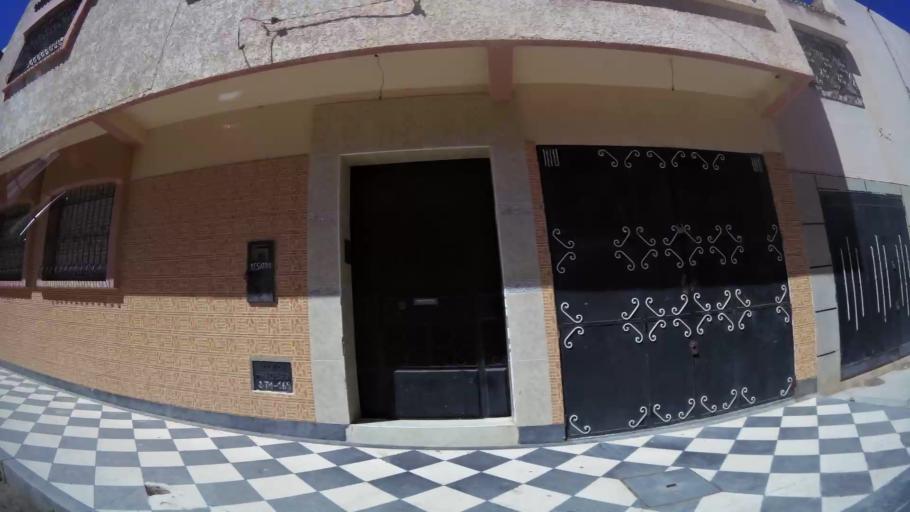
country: MA
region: Oriental
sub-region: Oujda-Angad
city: Oujda
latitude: 34.6577
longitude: -1.8912
